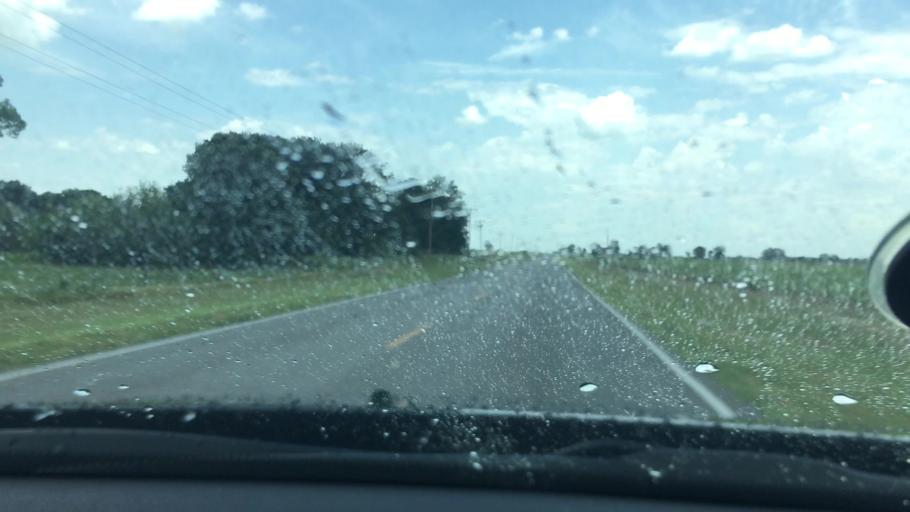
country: US
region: Oklahoma
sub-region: Carter County
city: Wilson
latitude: 33.9403
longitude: -97.4023
